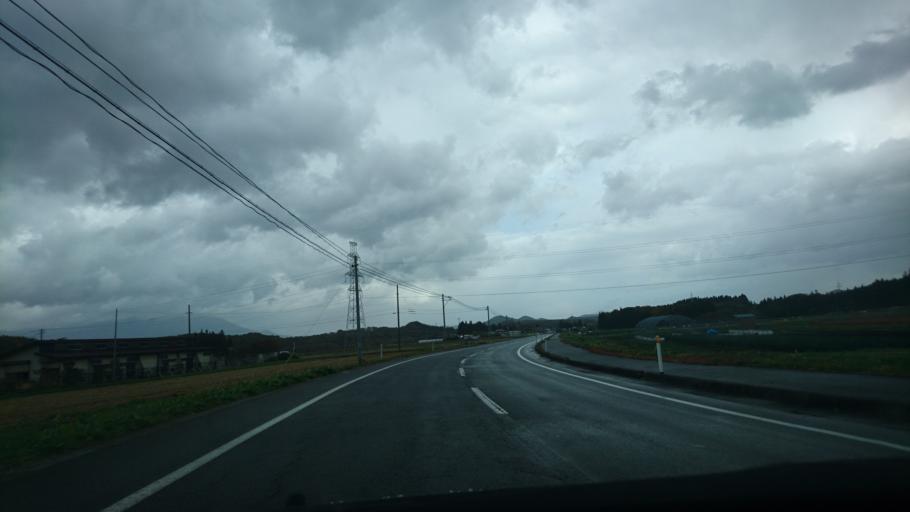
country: JP
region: Iwate
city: Shizukuishi
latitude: 39.6547
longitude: 140.9572
